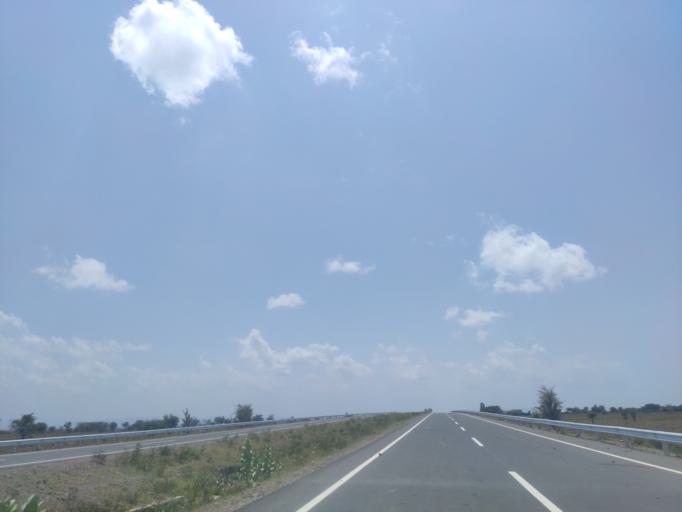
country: ET
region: Oromiya
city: Mojo
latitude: 8.3576
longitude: 38.9880
